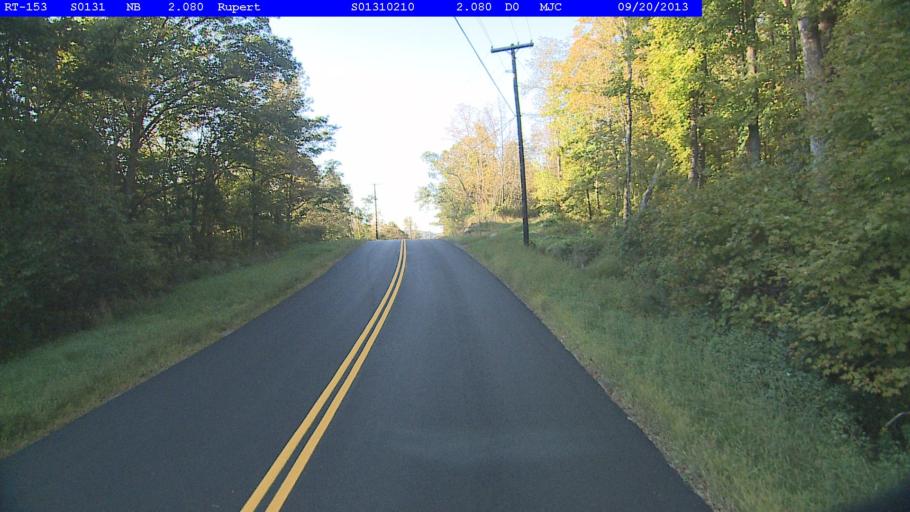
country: US
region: New York
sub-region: Washington County
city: Granville
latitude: 43.2850
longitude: -73.2385
